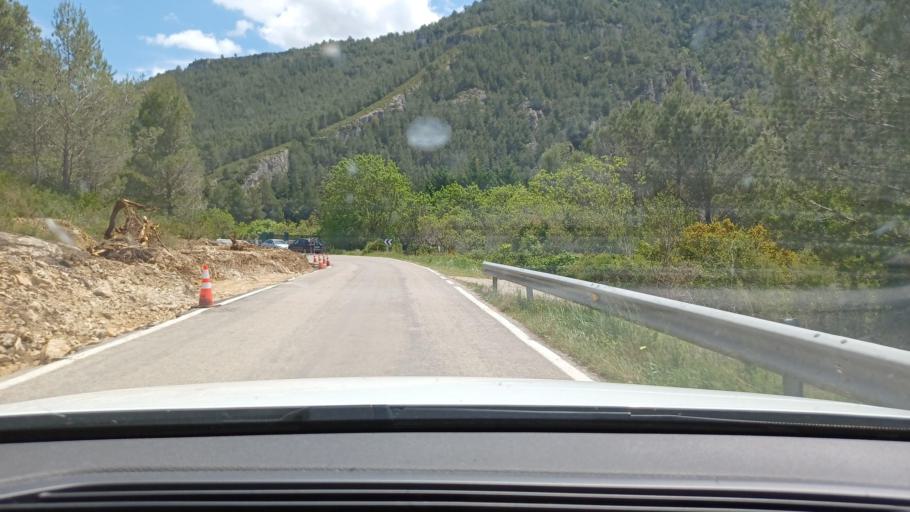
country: ES
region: Valencia
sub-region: Provincia de Castello
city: Rosell
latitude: 40.6689
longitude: 0.2493
